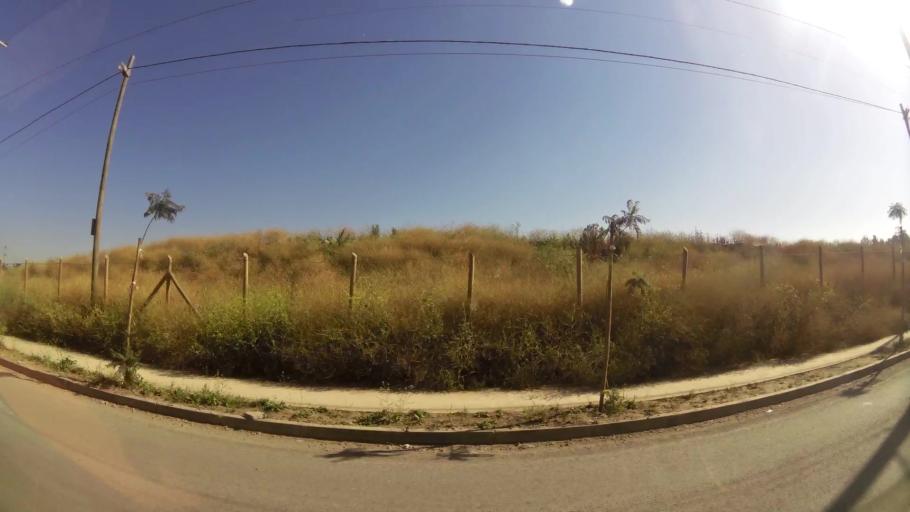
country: CL
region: Santiago Metropolitan
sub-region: Provincia de Maipo
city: San Bernardo
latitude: -33.6087
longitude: -70.6793
